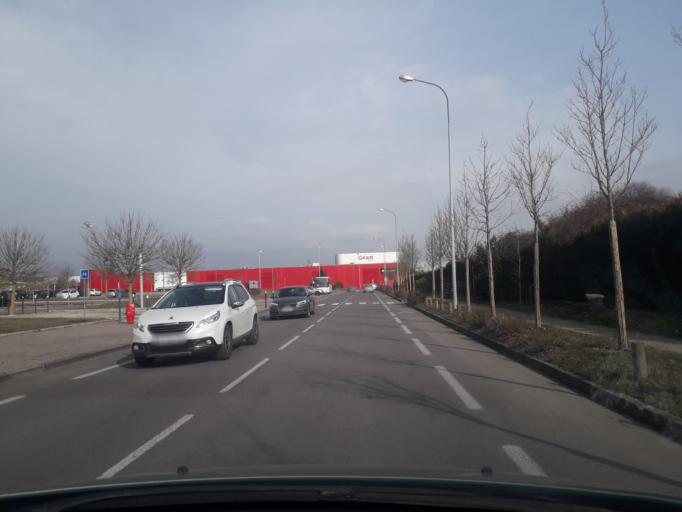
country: FR
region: Bourgogne
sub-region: Departement de la Cote-d'Or
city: Fontaine-les-Dijon
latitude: 47.3541
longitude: 5.0308
